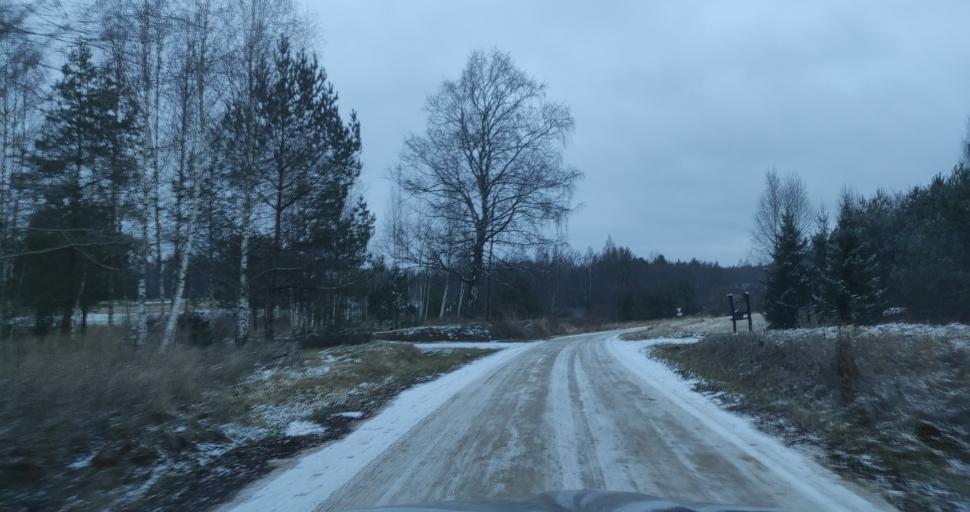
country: LV
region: Kuldigas Rajons
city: Kuldiga
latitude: 56.9796
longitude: 22.0516
